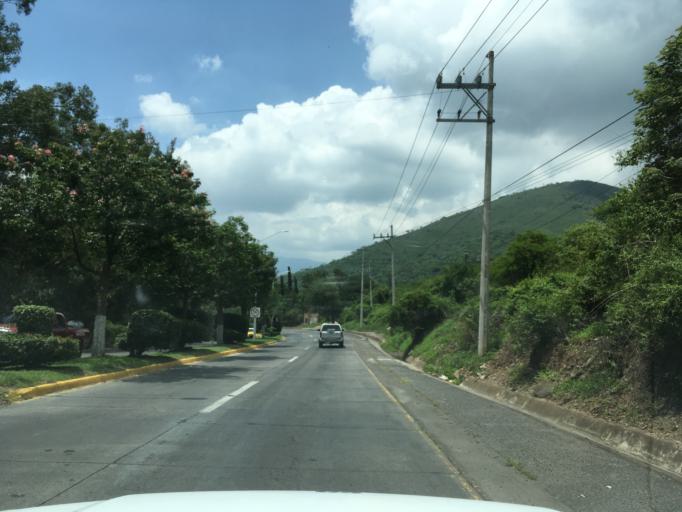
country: MX
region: Jalisco
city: Tlajomulco de Zuniga
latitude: 20.4860
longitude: -103.4572
